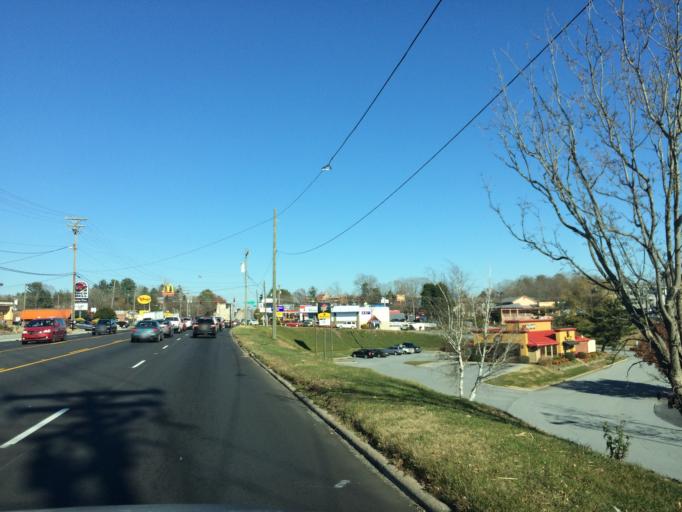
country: US
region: North Carolina
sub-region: Henderson County
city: Hendersonville
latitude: 35.3358
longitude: -82.4466
